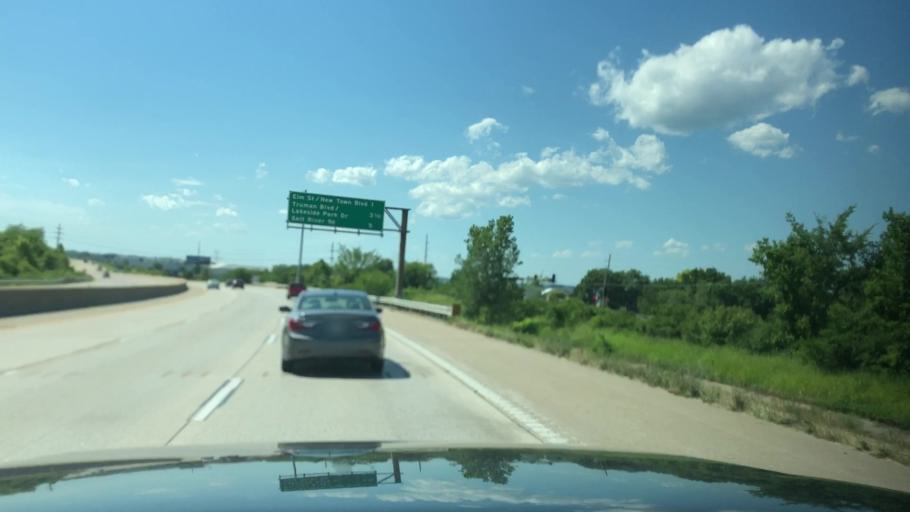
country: US
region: Missouri
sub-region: Saint Charles County
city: Saint Charles
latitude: 38.8180
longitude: -90.4968
